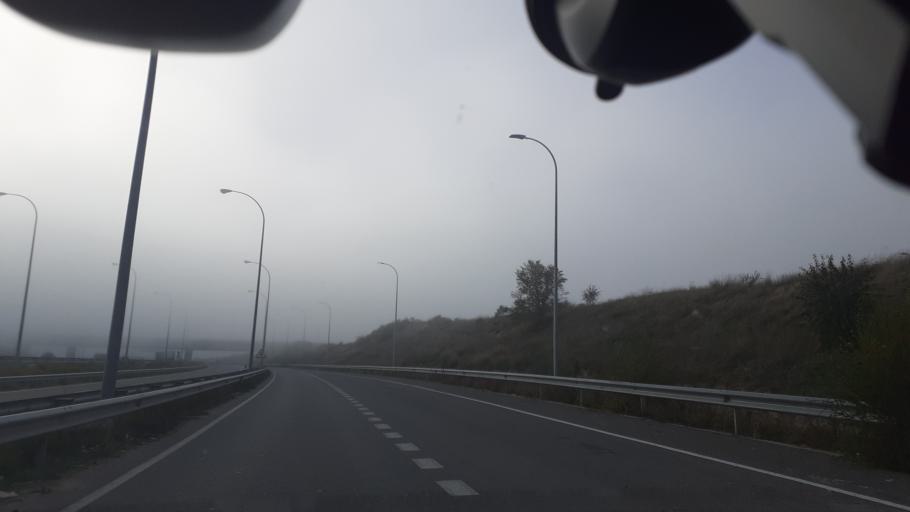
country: ES
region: Madrid
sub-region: Provincia de Madrid
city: Coslada
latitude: 40.4112
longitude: -3.5569
